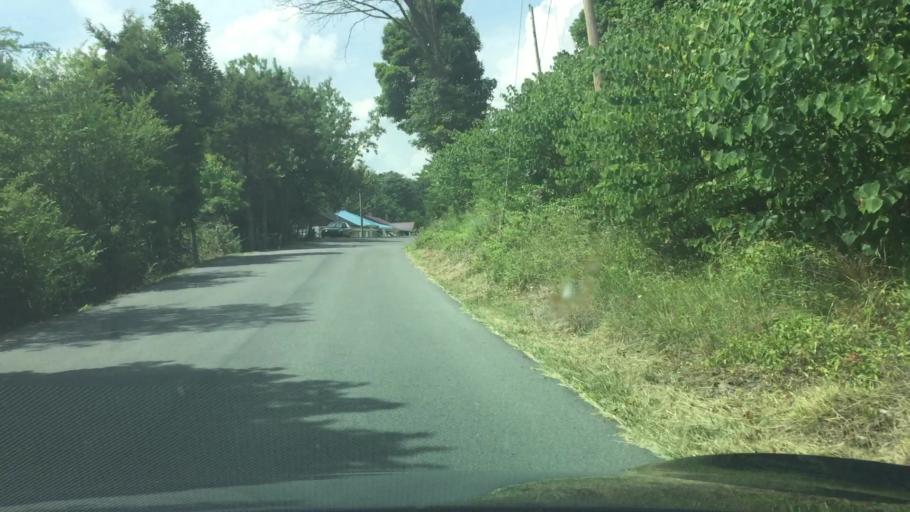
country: US
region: Virginia
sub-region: Wythe County
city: Wytheville
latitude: 36.9395
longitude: -81.0786
